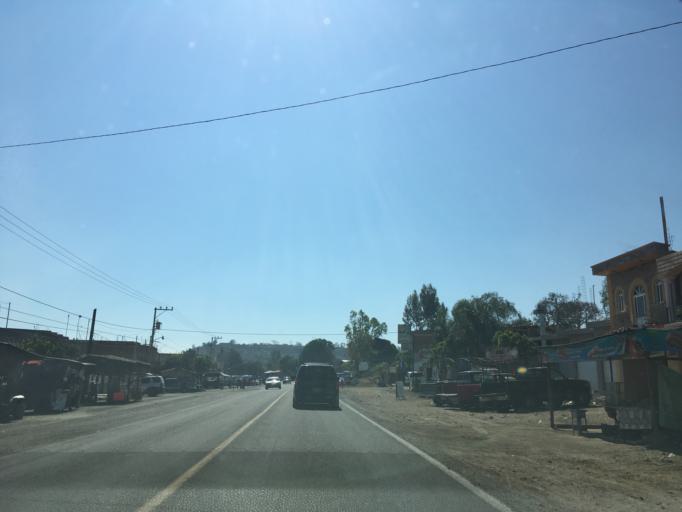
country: MX
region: Michoacan
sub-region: Indaparapeo
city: San Lucas Pio
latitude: 19.7940
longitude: -100.9274
